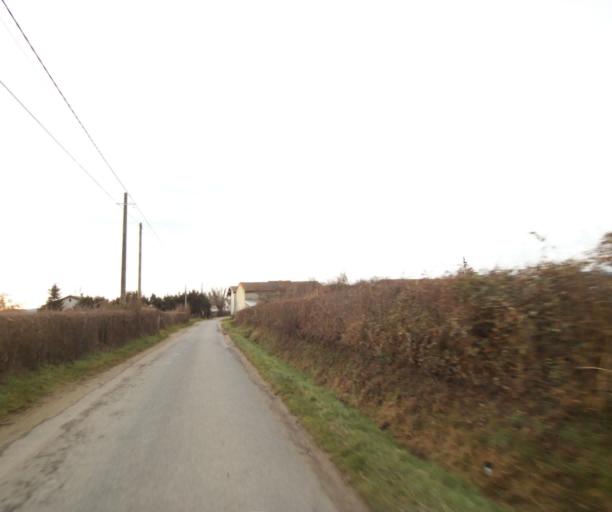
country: FR
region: Rhone-Alpes
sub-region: Departement de la Loire
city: Sury-le-Comtal
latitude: 45.5302
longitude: 4.1663
